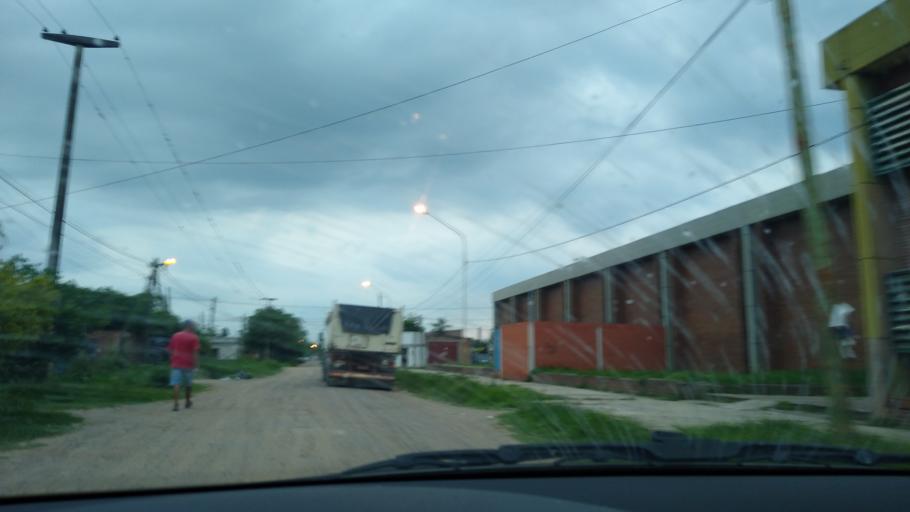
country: AR
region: Chaco
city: Barranqueras
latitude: -27.4879
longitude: -58.9359
